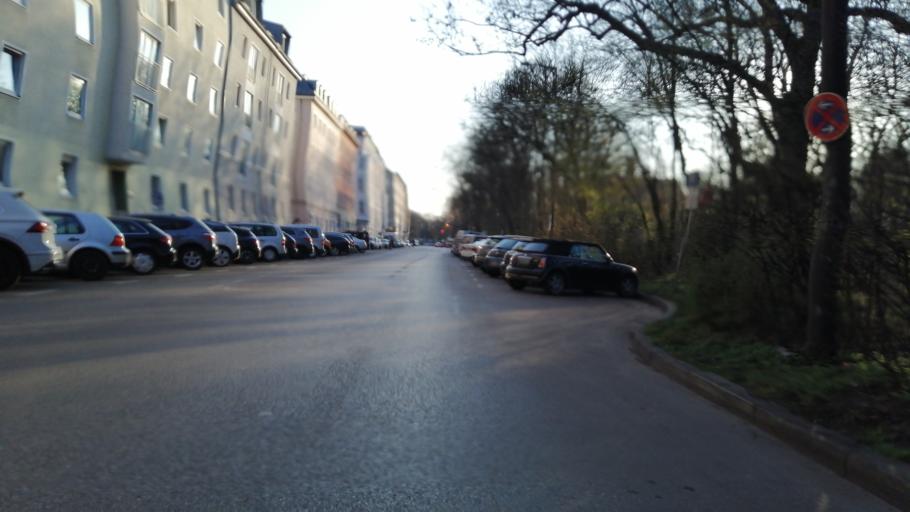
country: DE
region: Bavaria
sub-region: Upper Bavaria
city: Munich
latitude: 48.1223
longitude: 11.5736
